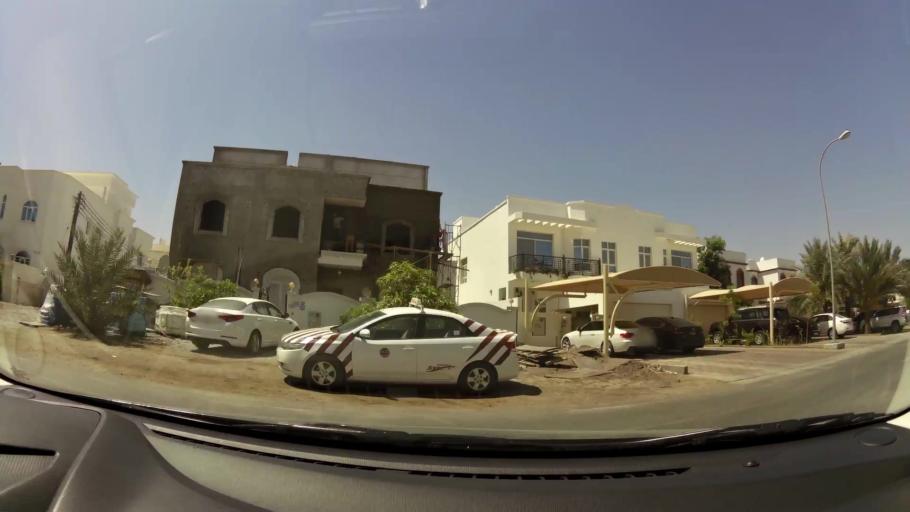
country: OM
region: Muhafazat Masqat
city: As Sib al Jadidah
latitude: 23.6226
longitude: 58.2575
